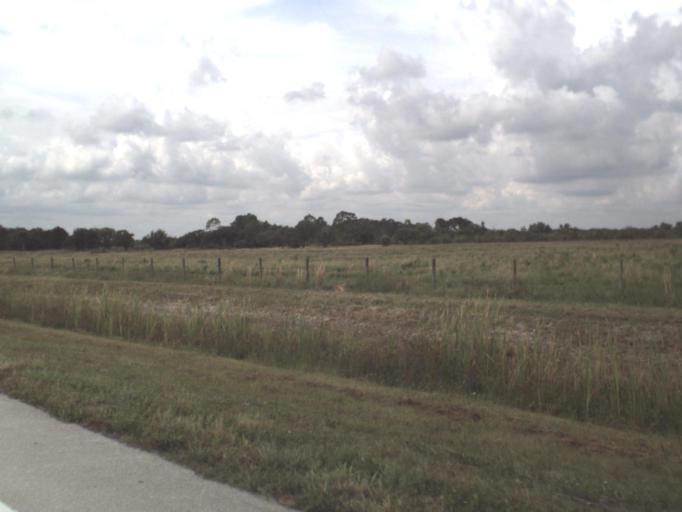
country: US
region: Florida
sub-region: Hendry County
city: Port LaBelle
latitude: 26.8216
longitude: -81.4050
